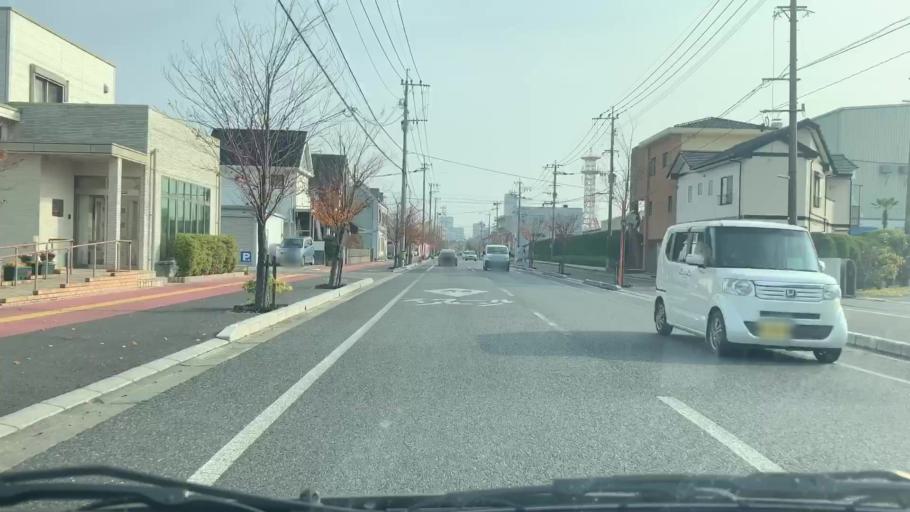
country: JP
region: Saga Prefecture
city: Saga-shi
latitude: 33.2632
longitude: 130.2856
